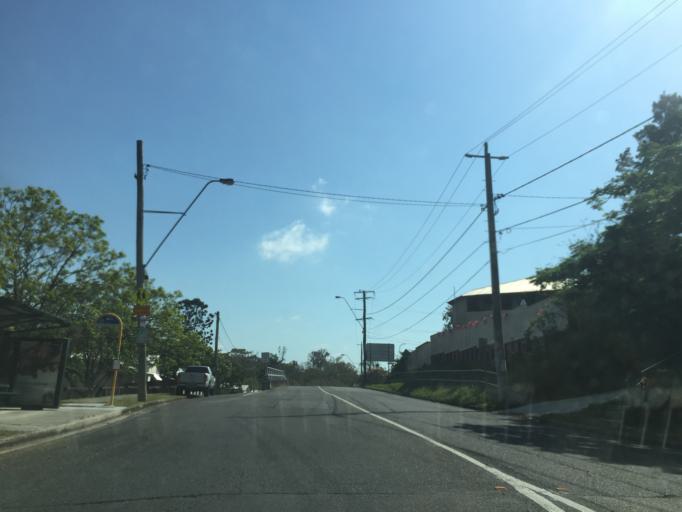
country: AU
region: Queensland
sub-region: Brisbane
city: Milton
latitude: -27.4674
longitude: 152.9883
